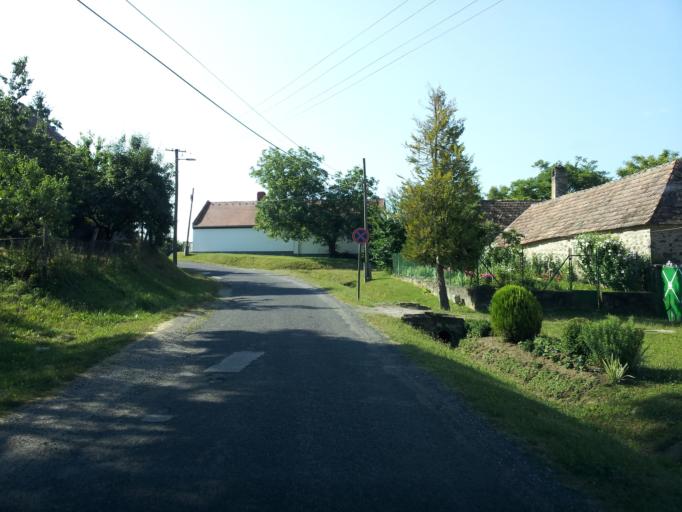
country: HU
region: Zala
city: Cserszegtomaj
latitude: 46.8893
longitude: 17.2272
